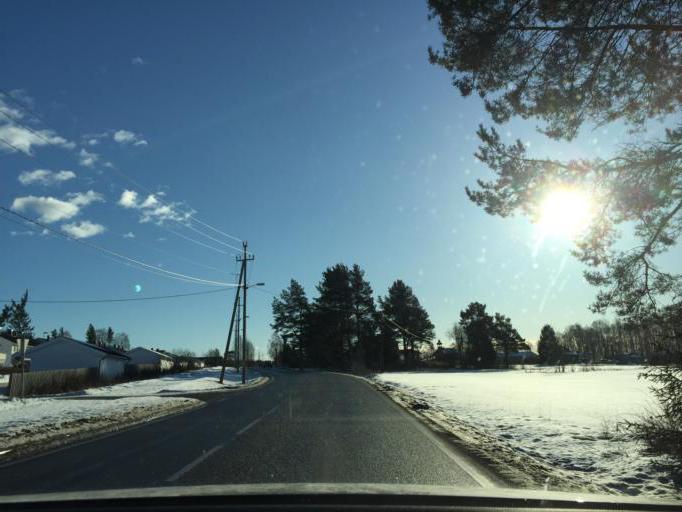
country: NO
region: Akershus
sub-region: Nes
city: Arnes
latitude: 60.1100
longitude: 11.4753
